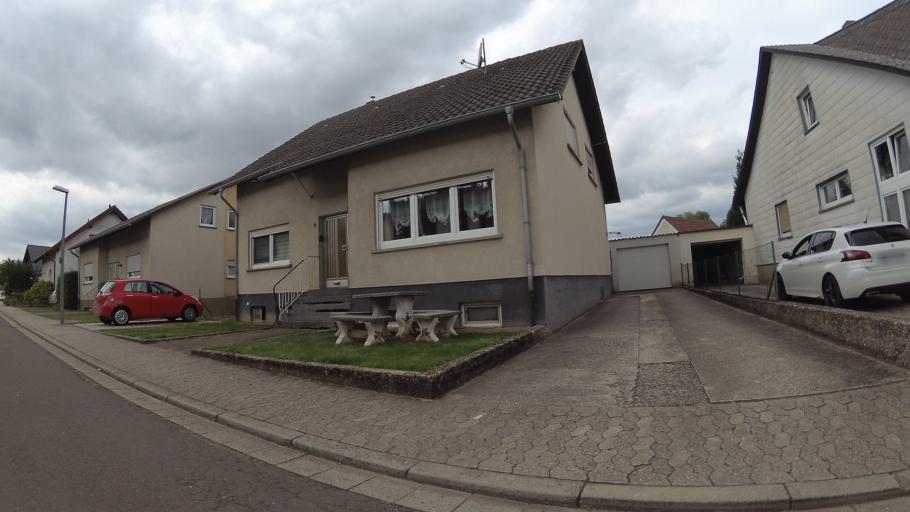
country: FR
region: Lorraine
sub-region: Departement de la Moselle
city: Sarreinsming
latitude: 49.1504
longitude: 7.1152
